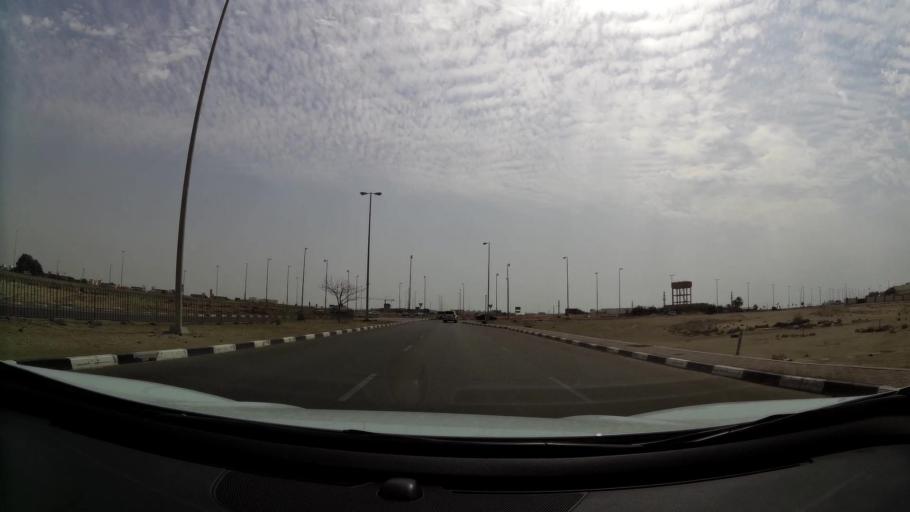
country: AE
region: Abu Dhabi
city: Abu Dhabi
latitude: 24.5427
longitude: 54.6840
